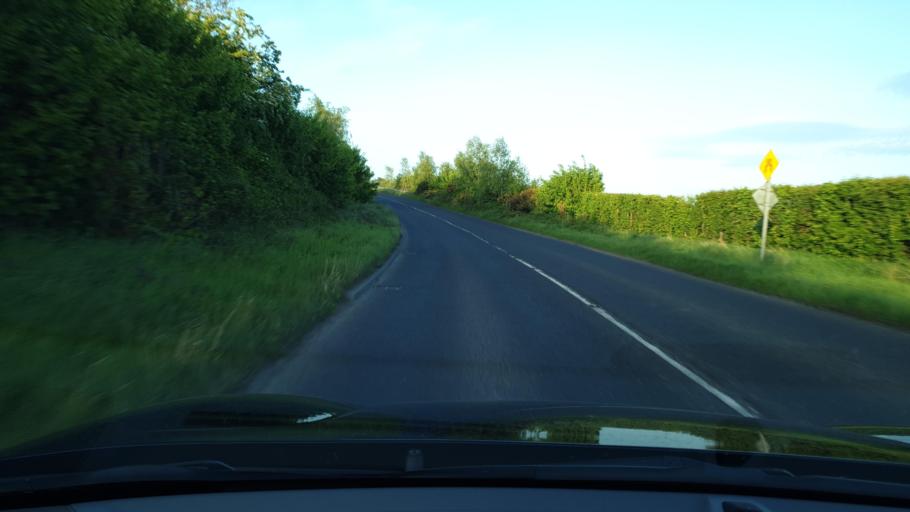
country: IE
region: Leinster
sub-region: An Mhi
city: Ashbourne
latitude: 53.5099
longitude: -6.4242
